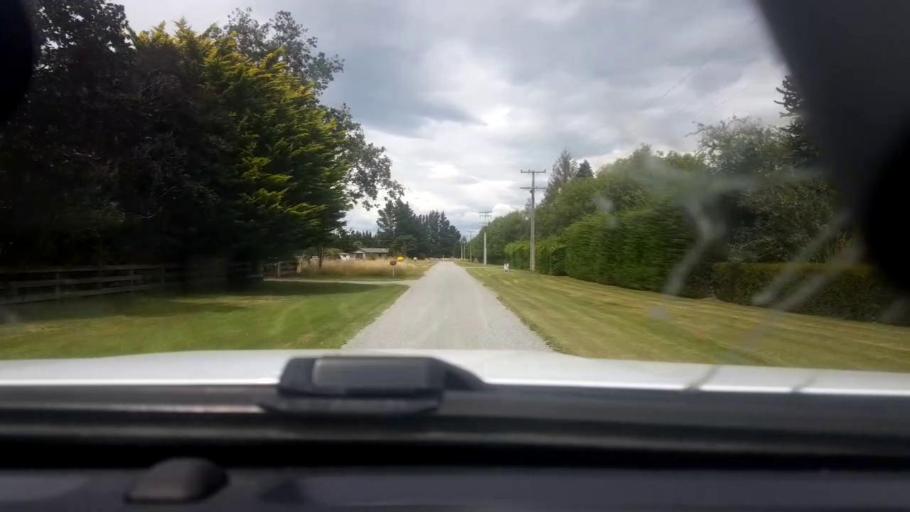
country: NZ
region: Canterbury
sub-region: Timaru District
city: Pleasant Point
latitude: -44.1424
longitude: 171.2894
